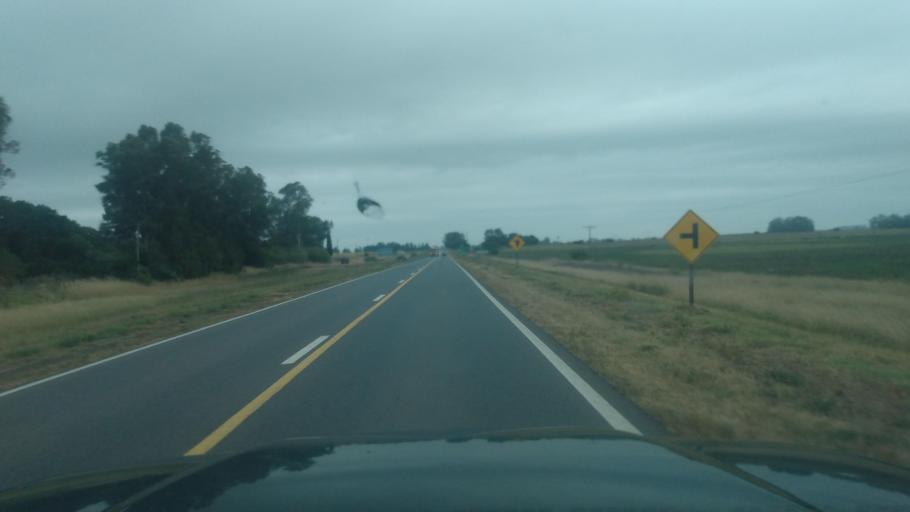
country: AR
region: Buenos Aires
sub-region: Partido de Bragado
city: Bragado
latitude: -35.2809
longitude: -60.5919
